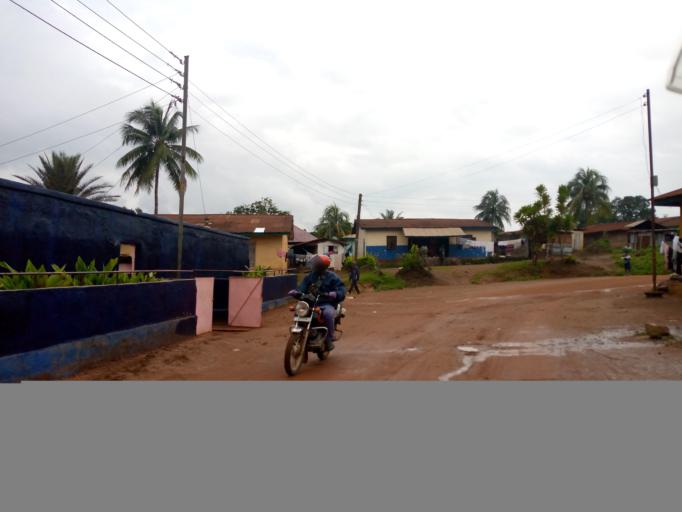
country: SL
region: Eastern Province
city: Kenema
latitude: 7.8625
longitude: -11.1920
